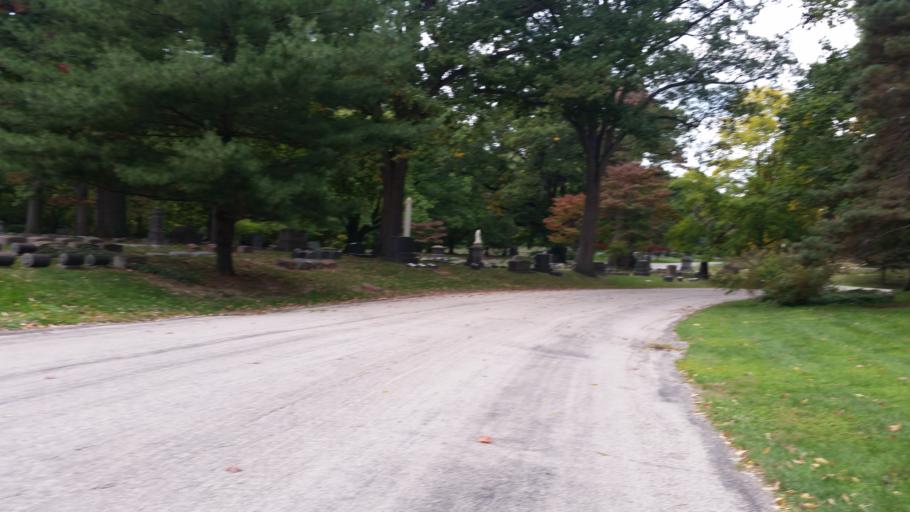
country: US
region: Ohio
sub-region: Cuyahoga County
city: East Cleveland
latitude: 41.5126
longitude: -81.5938
